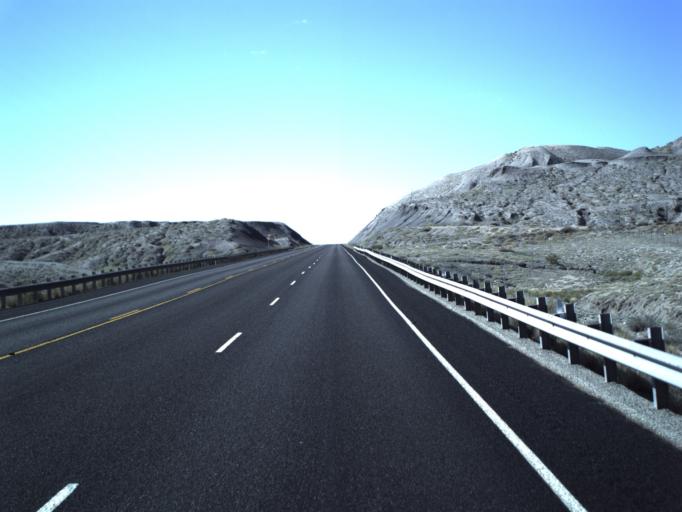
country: US
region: Utah
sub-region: Emery County
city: Ferron
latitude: 39.0432
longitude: -111.1249
